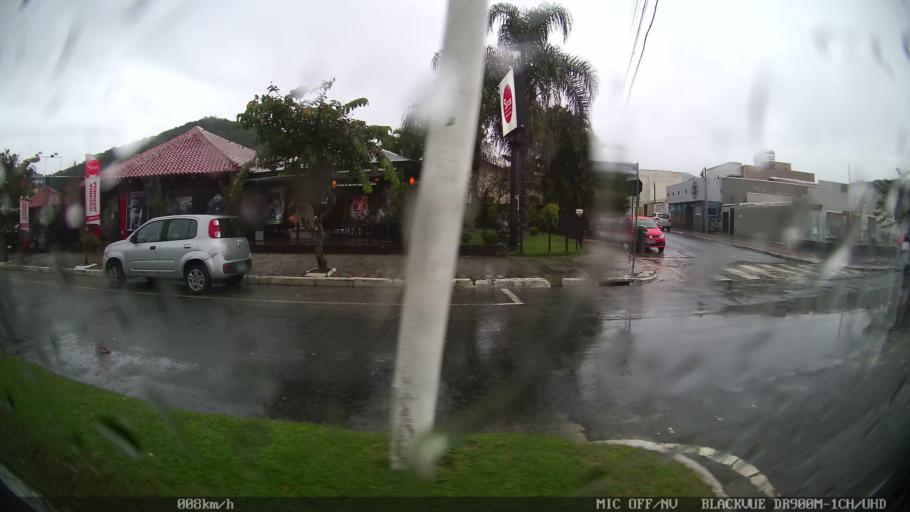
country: BR
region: Santa Catarina
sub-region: Balneario Camboriu
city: Balneario Camboriu
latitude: -26.9570
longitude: -48.6329
